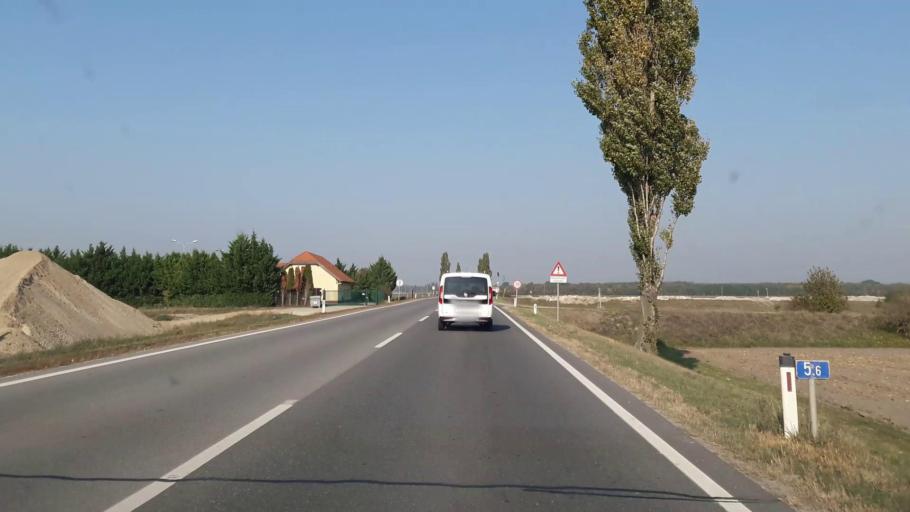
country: AT
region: Lower Austria
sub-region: Politischer Bezirk Ganserndorf
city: Engelhartstetten
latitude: 48.1860
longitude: 16.8947
